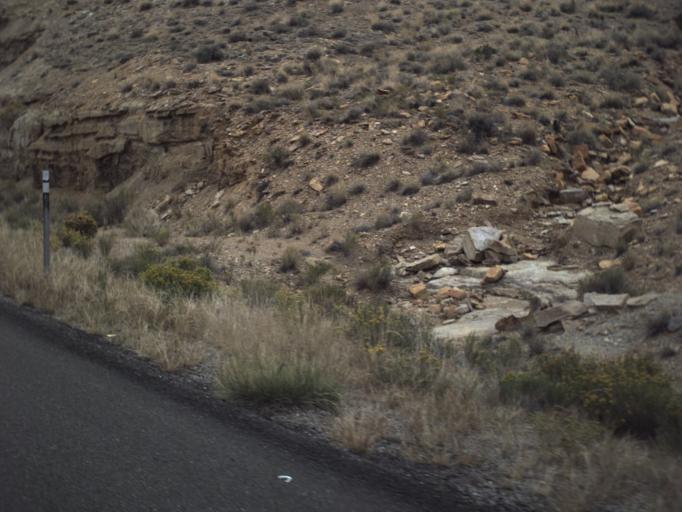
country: US
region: Utah
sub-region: Emery County
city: Castle Dale
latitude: 38.9376
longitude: -110.4806
